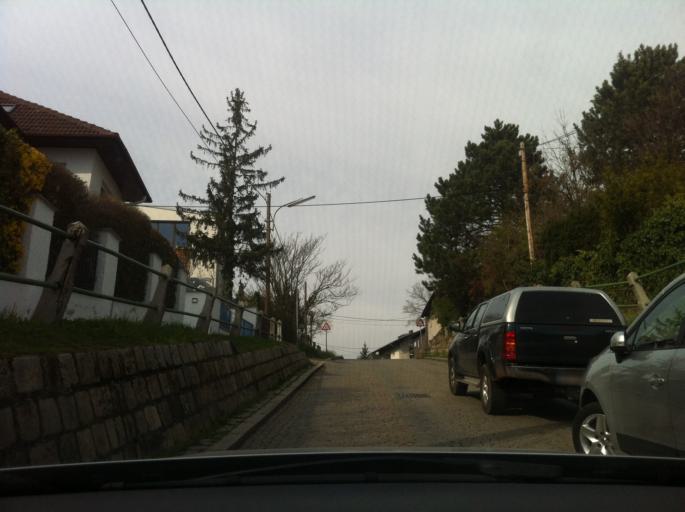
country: AT
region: Lower Austria
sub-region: Politischer Bezirk Modling
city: Perchtoldsdorf
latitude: 48.1984
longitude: 16.2775
